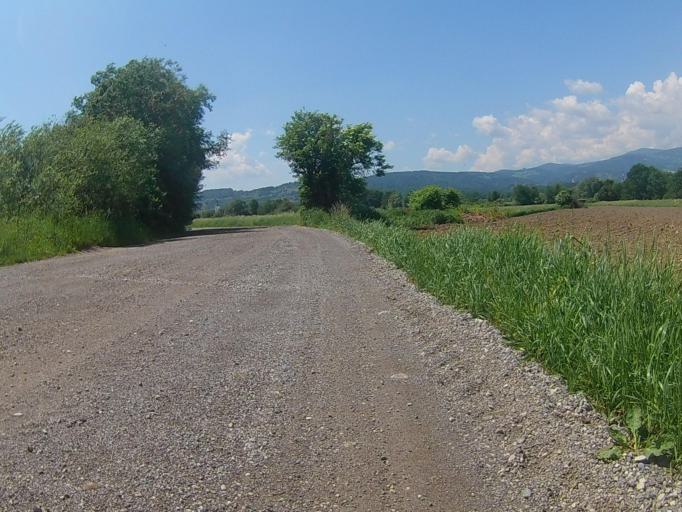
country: SI
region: Hoce-Slivnica
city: Radizel
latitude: 46.4859
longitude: 15.6665
